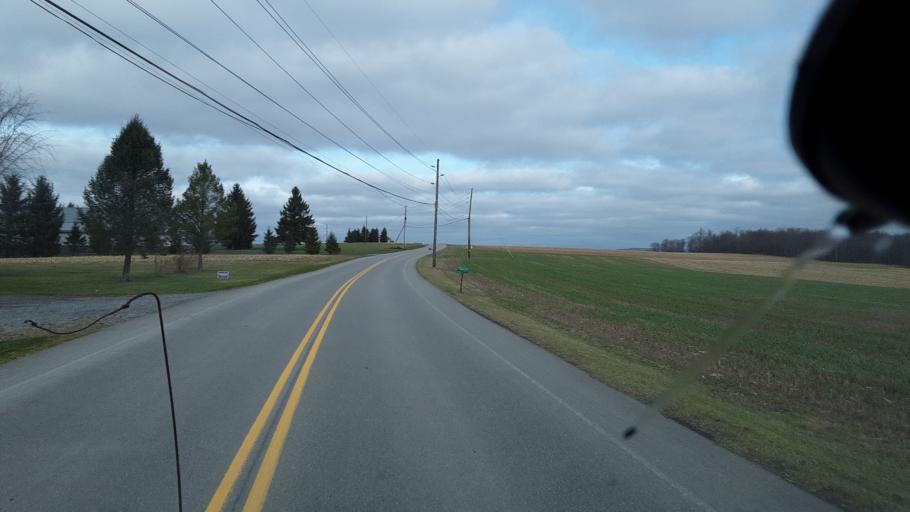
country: US
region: Pennsylvania
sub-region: Potter County
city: Galeton
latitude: 41.8759
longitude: -77.7639
